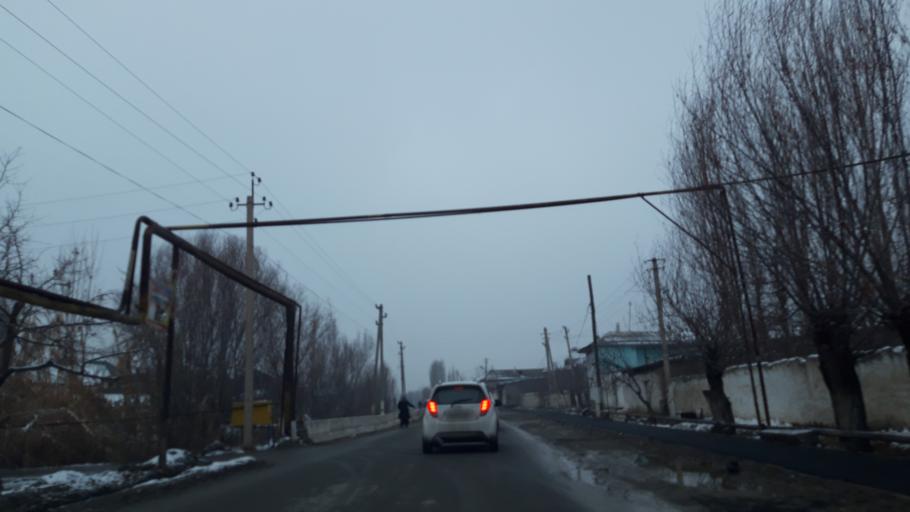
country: UZ
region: Andijon
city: Andijon
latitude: 40.7607
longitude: 72.3077
